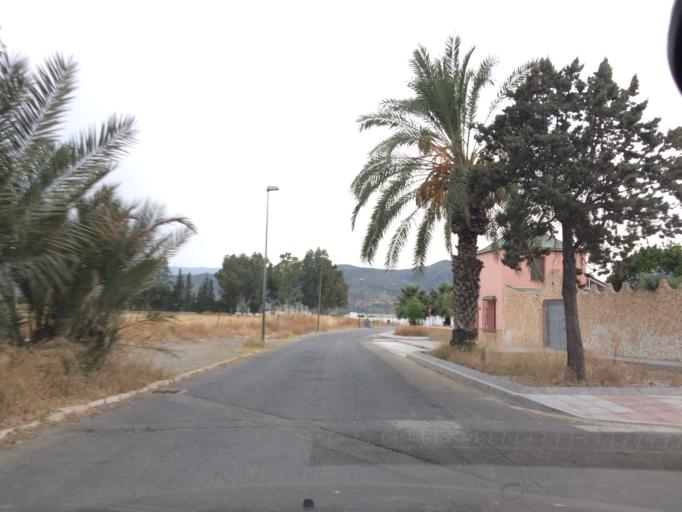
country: ES
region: Andalusia
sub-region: Provincia de Malaga
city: Estacion de Cartama
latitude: 36.7300
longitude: -4.5694
